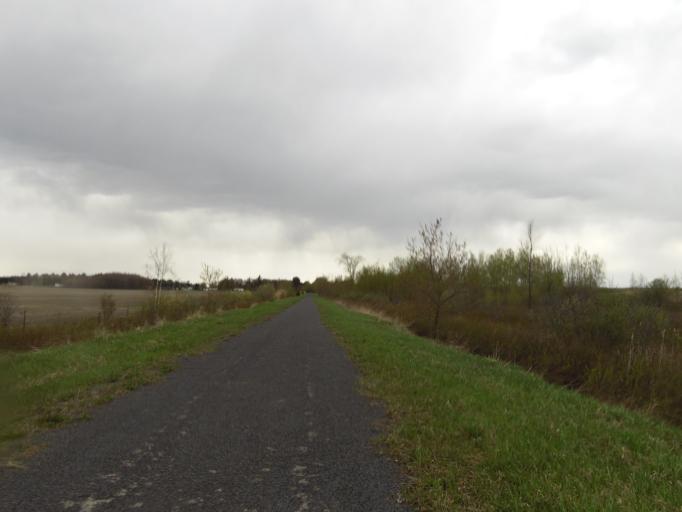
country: CA
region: Ontario
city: Bourget
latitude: 45.4449
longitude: -75.1327
